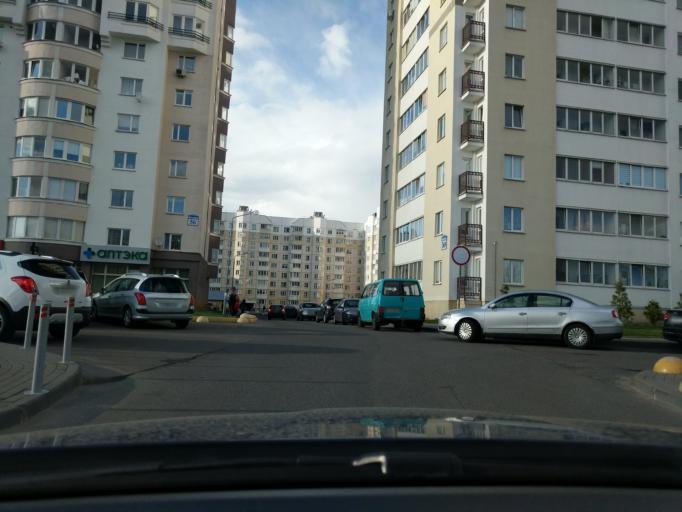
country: BY
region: Minsk
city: Novoye Medvezhino
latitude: 53.9167
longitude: 27.4613
